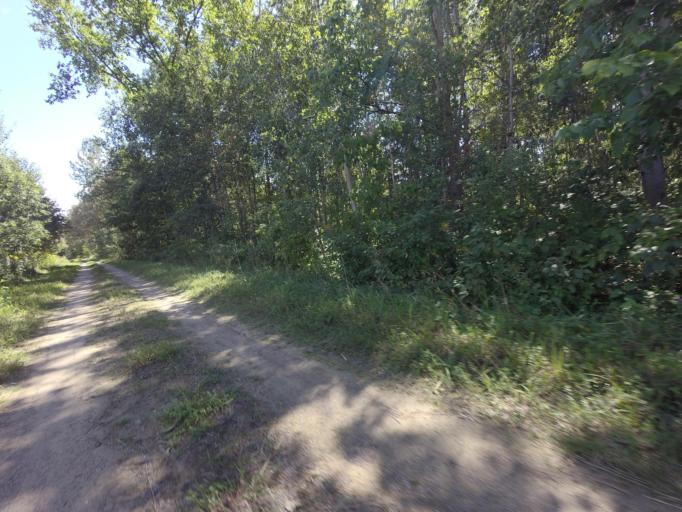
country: CA
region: Ontario
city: Orangeville
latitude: 43.7735
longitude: -80.1917
